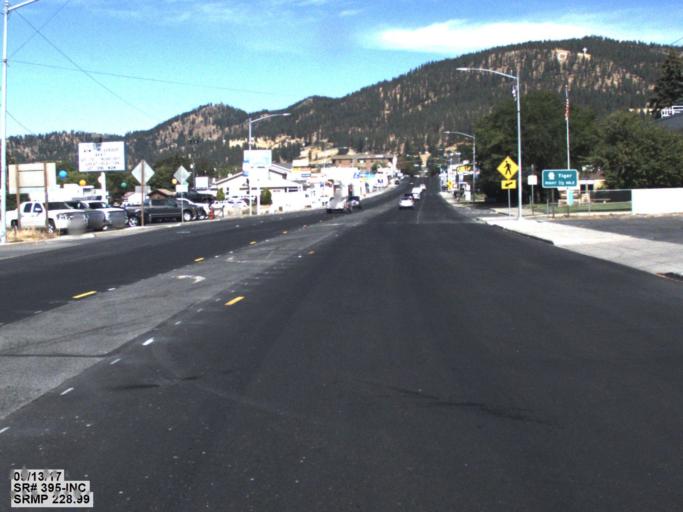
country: US
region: Washington
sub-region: Stevens County
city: Colville
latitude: 48.5372
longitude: -117.9057
